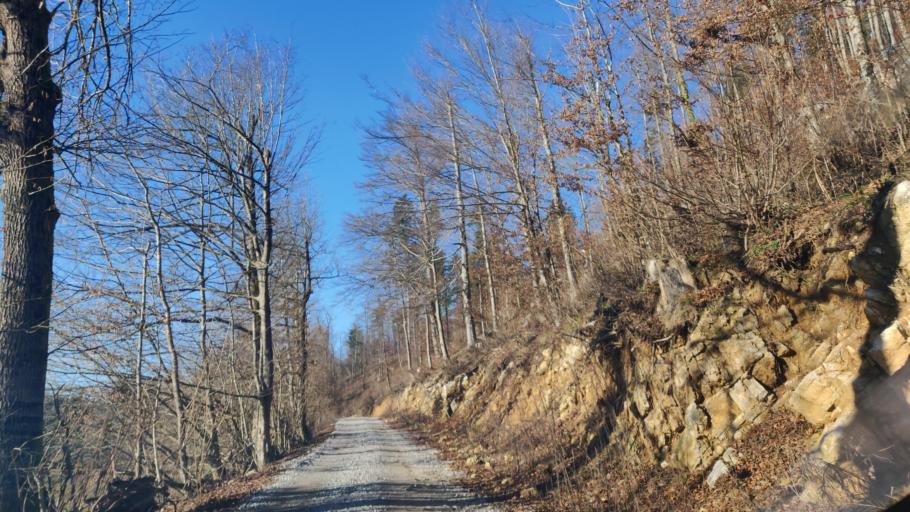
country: SI
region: Logatec
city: Logatec
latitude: 45.8703
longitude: 14.2216
